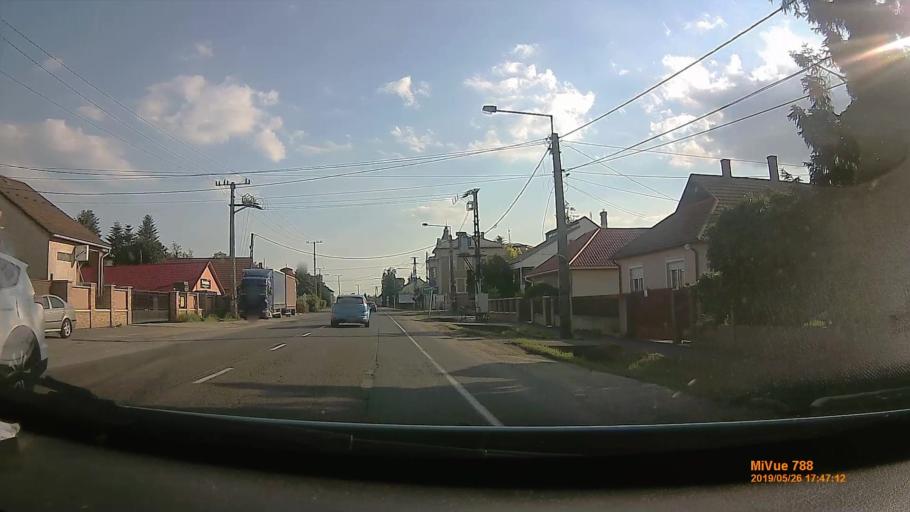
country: HU
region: Borsod-Abauj-Zemplen
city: Szikszo
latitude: 48.2035
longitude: 20.9349
